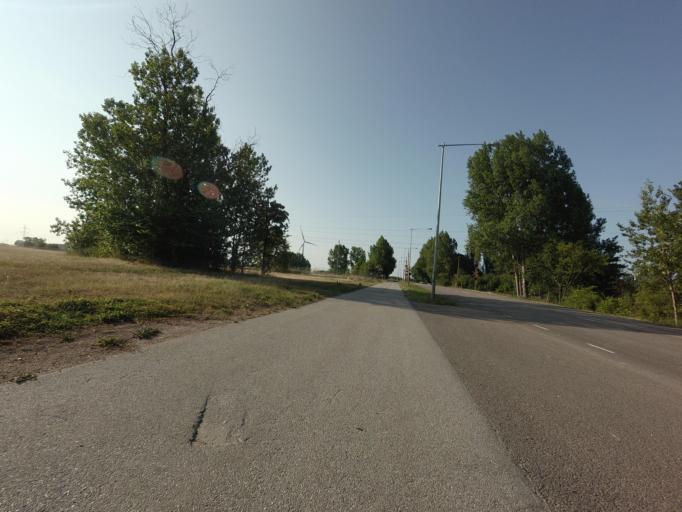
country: SE
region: Skane
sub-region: Landskrona
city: Landskrona
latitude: 55.8677
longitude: 12.8698
